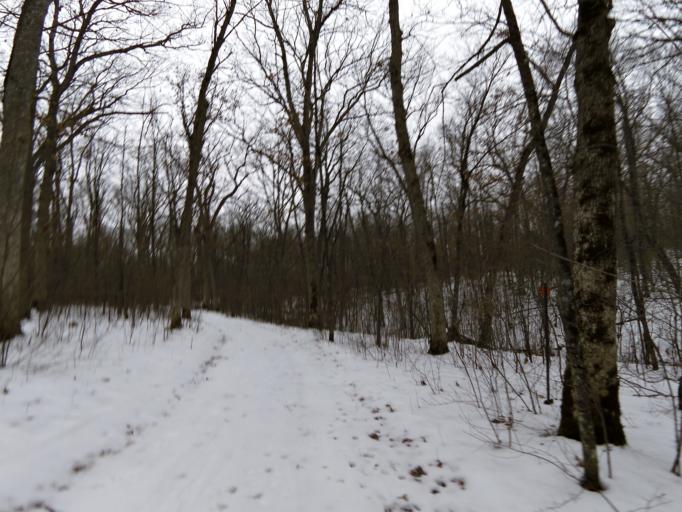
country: US
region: Wisconsin
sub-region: Pierce County
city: Prescott
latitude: 44.8054
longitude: -92.7887
